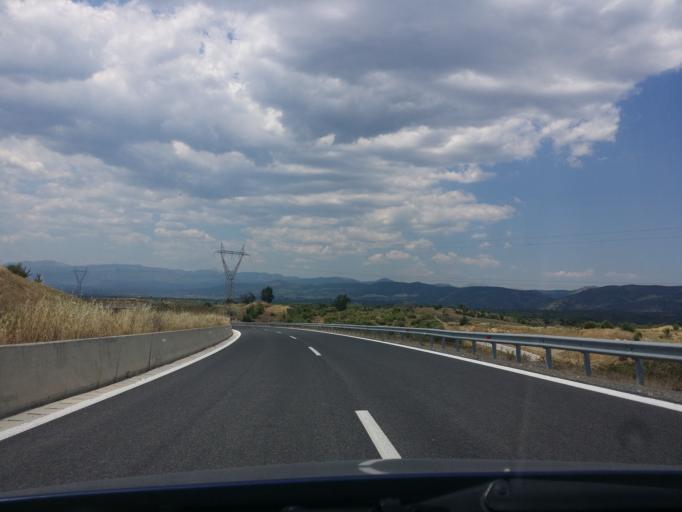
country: GR
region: Peloponnese
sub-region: Nomos Arkadias
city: Megalopoli
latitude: 37.3167
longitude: 22.1713
